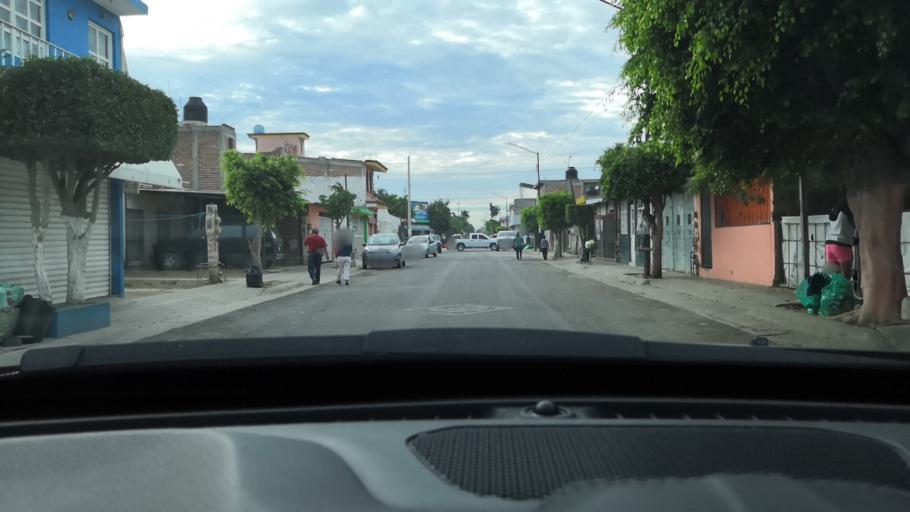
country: MX
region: Guanajuato
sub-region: Leon
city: Fraccionamiento Paraiso Real
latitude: 21.0997
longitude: -101.5886
